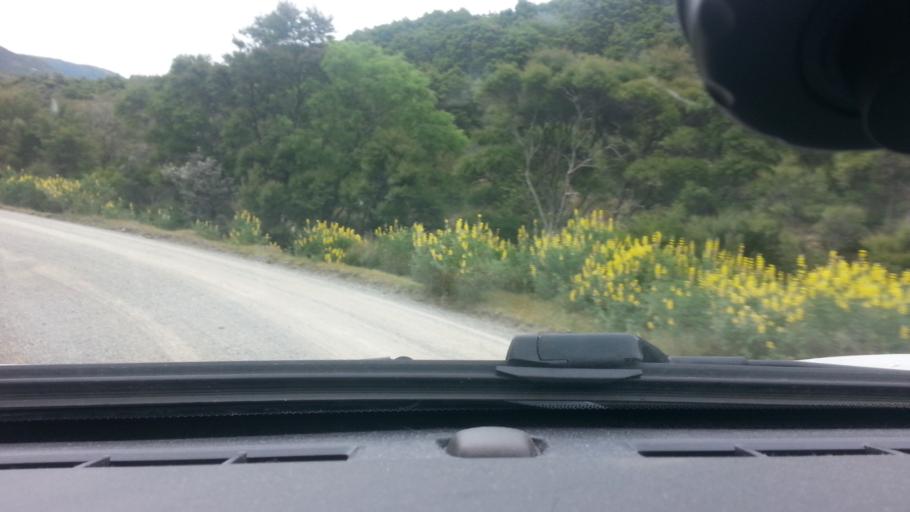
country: NZ
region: Wellington
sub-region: South Wairarapa District
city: Waipawa
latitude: -41.4799
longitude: 175.4360
